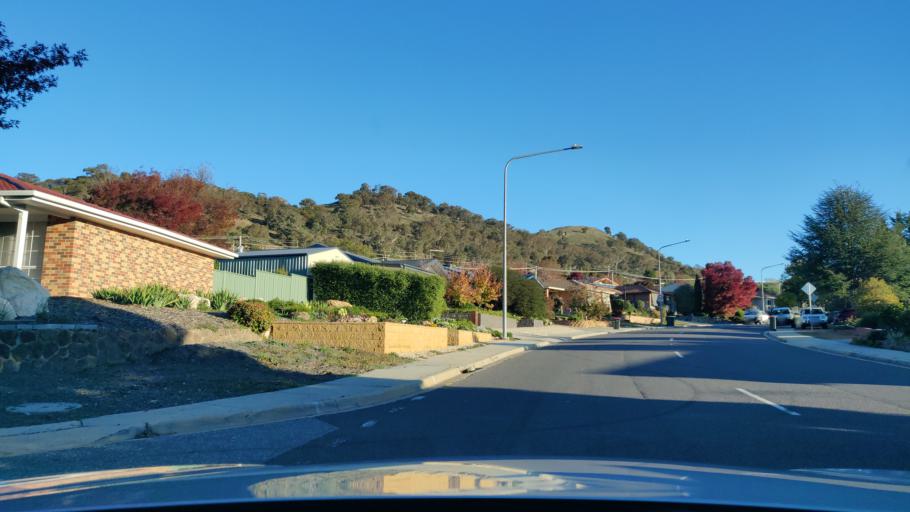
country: AU
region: Australian Capital Territory
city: Macarthur
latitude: -35.4486
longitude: 149.1245
